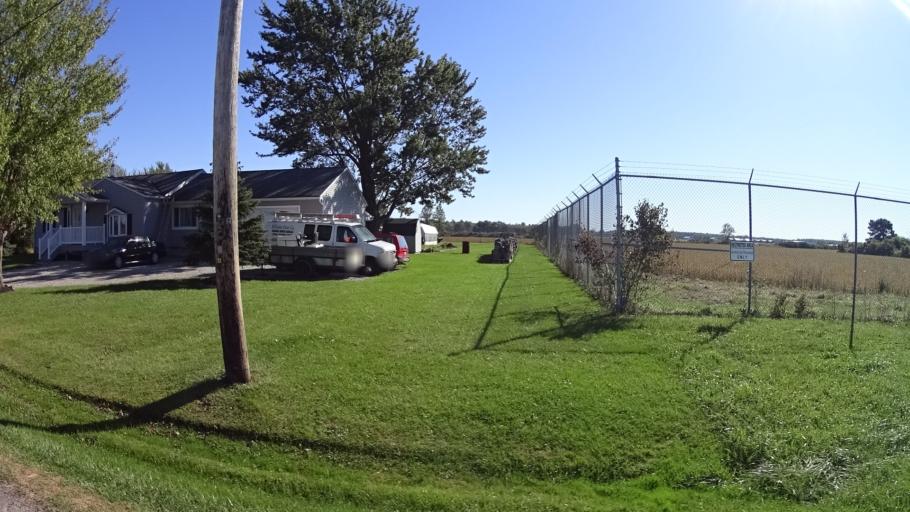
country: US
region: Ohio
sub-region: Lorain County
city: Elyria
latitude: 41.3523
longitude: -82.1688
